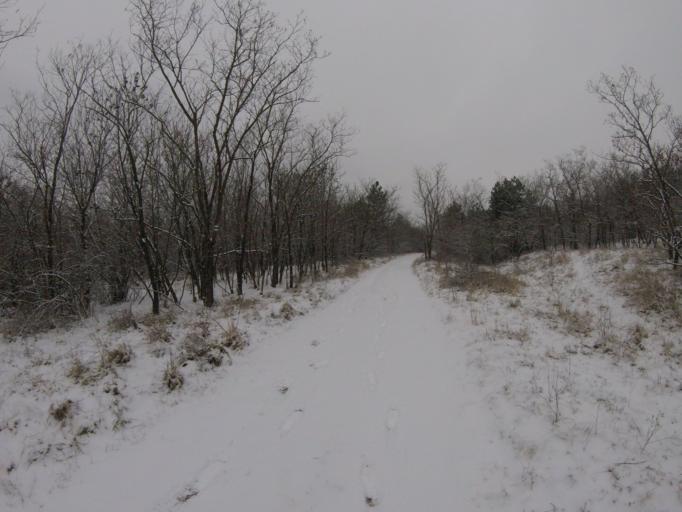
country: HU
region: Fejer
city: Pakozd
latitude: 47.2248
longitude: 18.5320
